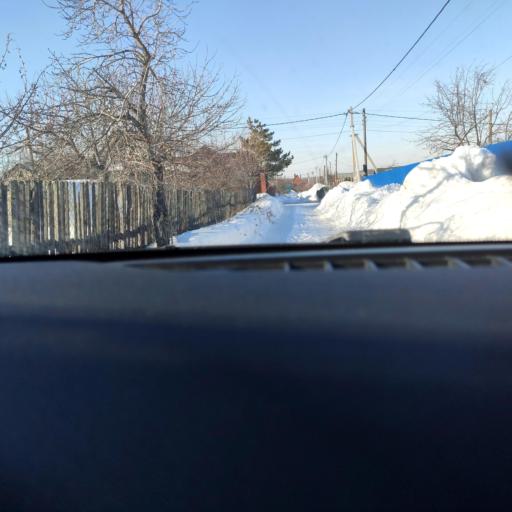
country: RU
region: Samara
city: Petra-Dubrava
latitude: 53.2861
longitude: 50.3075
